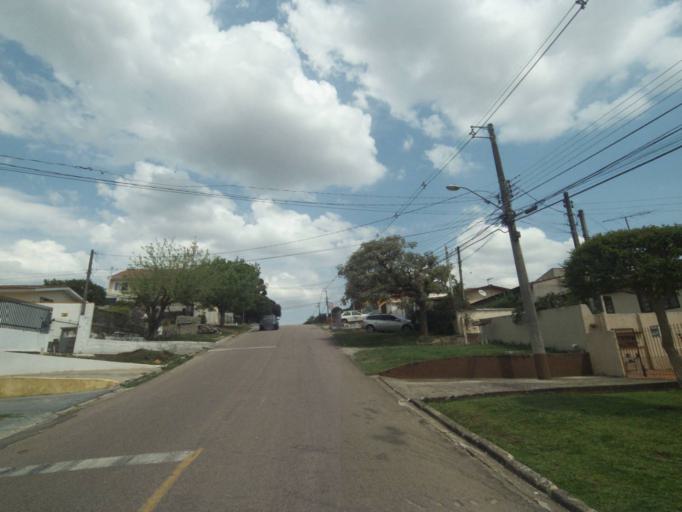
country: BR
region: Parana
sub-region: Pinhais
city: Pinhais
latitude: -25.3964
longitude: -49.1996
